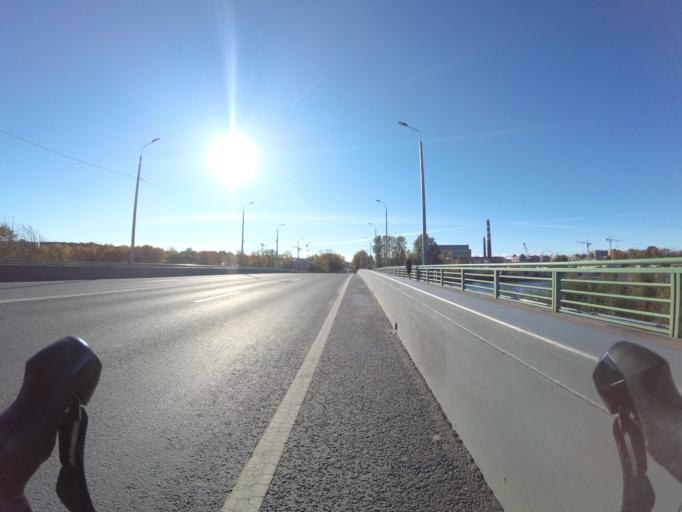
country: RU
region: Leningrad
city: Krestovskiy ostrov
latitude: 59.9654
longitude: 30.2551
